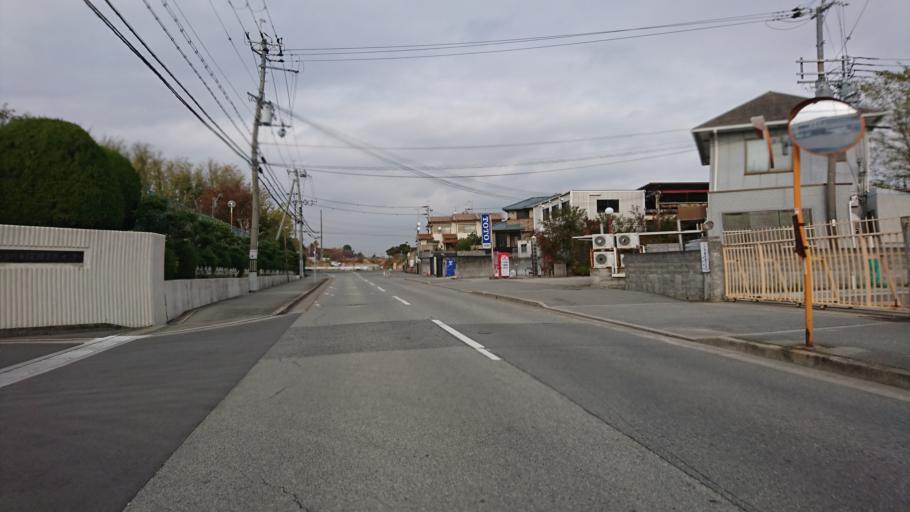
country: JP
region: Hyogo
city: Kakogawacho-honmachi
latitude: 34.7709
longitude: 134.8643
